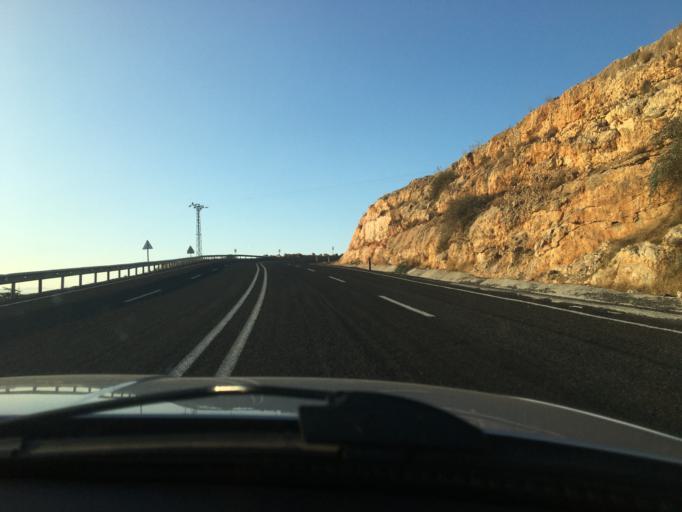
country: TR
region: Sanliurfa
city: Halfeti
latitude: 37.2396
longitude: 37.8838
